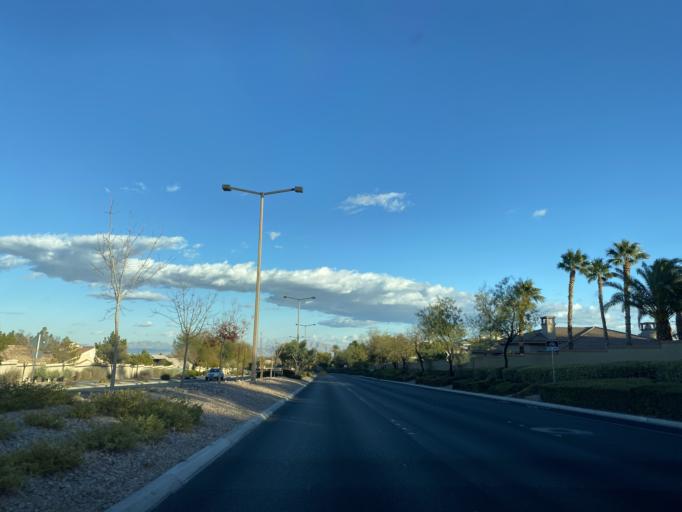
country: US
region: Nevada
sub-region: Clark County
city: Summerlin South
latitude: 36.2043
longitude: -115.3127
